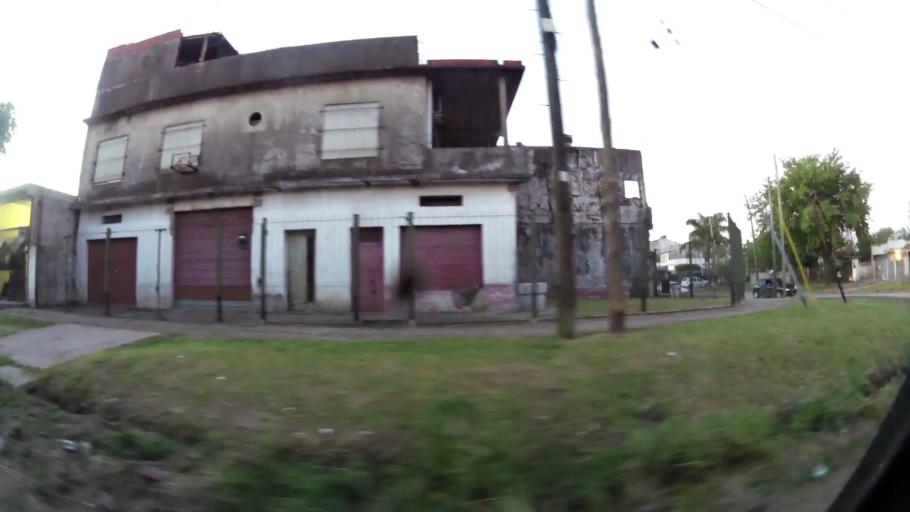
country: AR
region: Buenos Aires
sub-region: Partido de Almirante Brown
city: Adrogue
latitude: -34.7924
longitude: -58.3215
